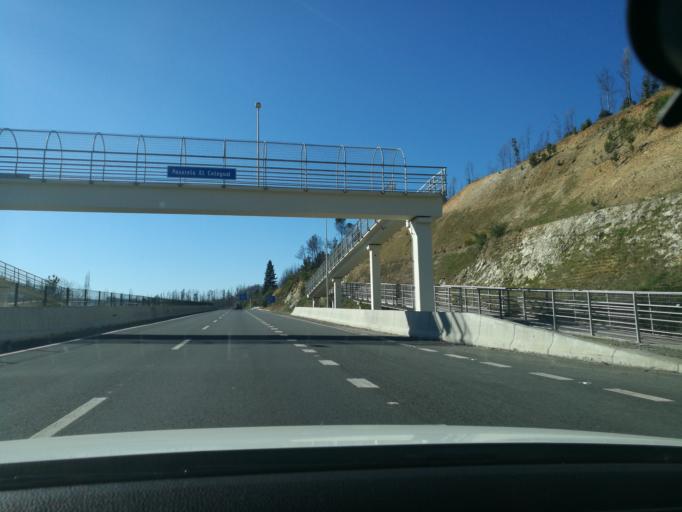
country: CL
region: Biobio
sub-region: Provincia de Concepcion
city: Chiguayante
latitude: -36.8560
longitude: -72.8896
